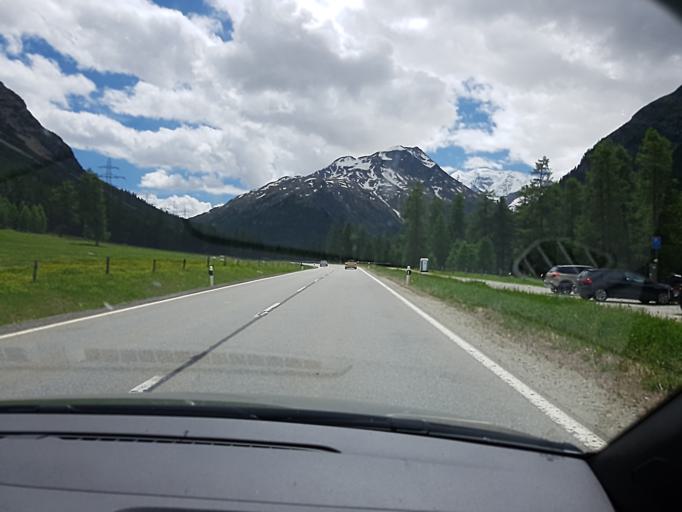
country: CH
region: Grisons
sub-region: Maloja District
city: Pontresina
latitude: 46.4693
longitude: 9.9285
